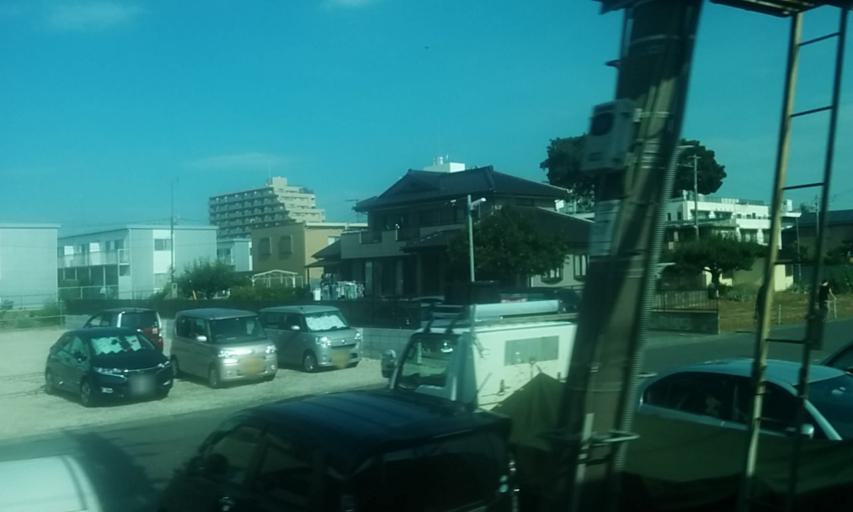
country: JP
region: Saitama
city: Shiraoka
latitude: 36.0126
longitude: 139.6662
